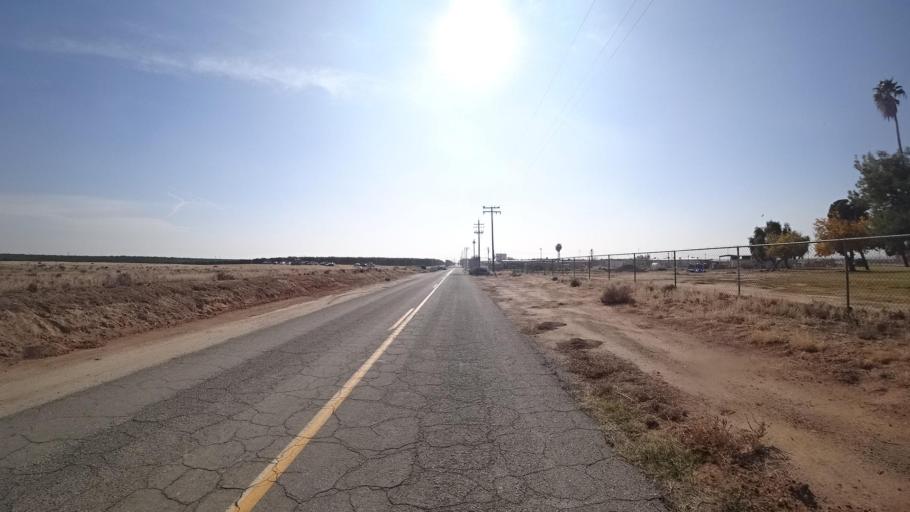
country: US
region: California
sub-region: Kern County
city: Oildale
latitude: 35.5157
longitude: -119.1086
